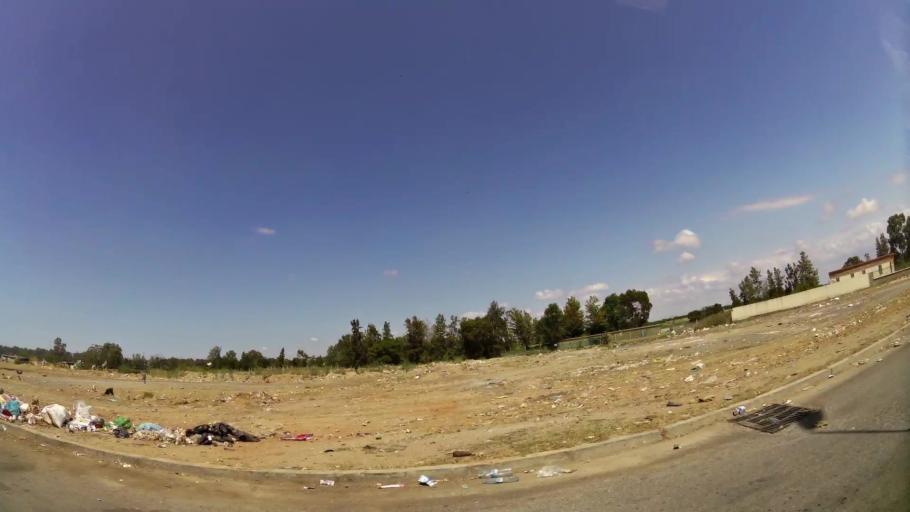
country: MA
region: Gharb-Chrarda-Beni Hssen
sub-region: Kenitra Province
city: Kenitra
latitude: 34.2485
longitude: -6.5373
